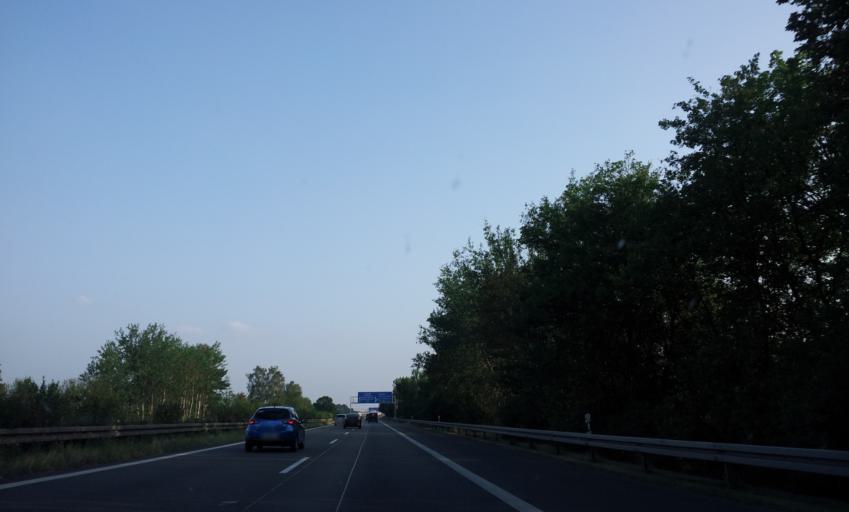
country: DE
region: Brandenburg
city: Bernau bei Berlin
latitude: 52.6391
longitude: 13.5662
